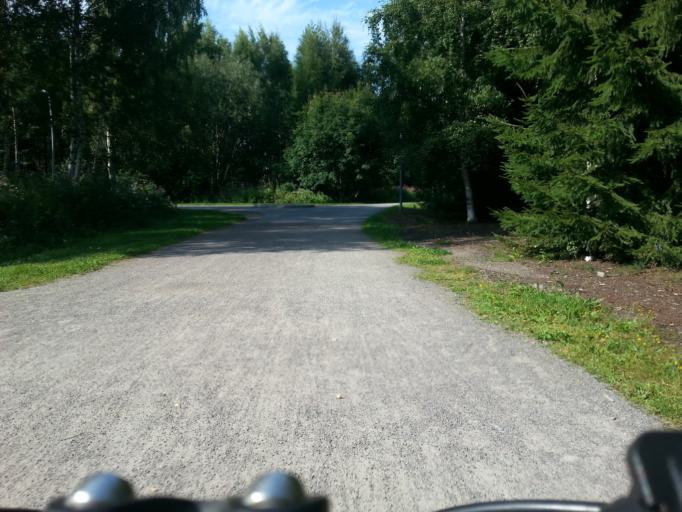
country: FI
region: Uusimaa
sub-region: Helsinki
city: Vantaa
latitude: 60.2368
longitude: 24.9940
